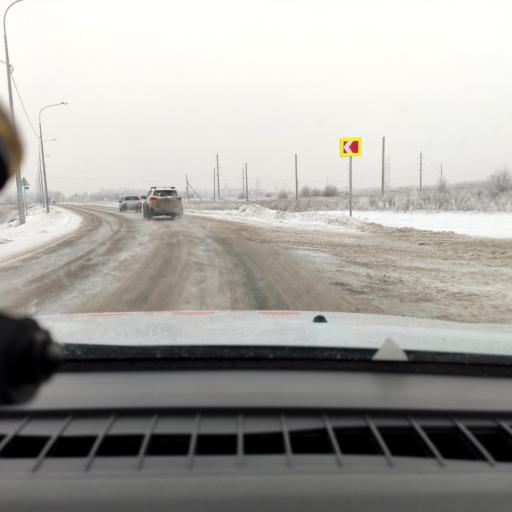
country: RU
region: Samara
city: Dubovyy Umet
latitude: 53.0815
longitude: 50.2320
